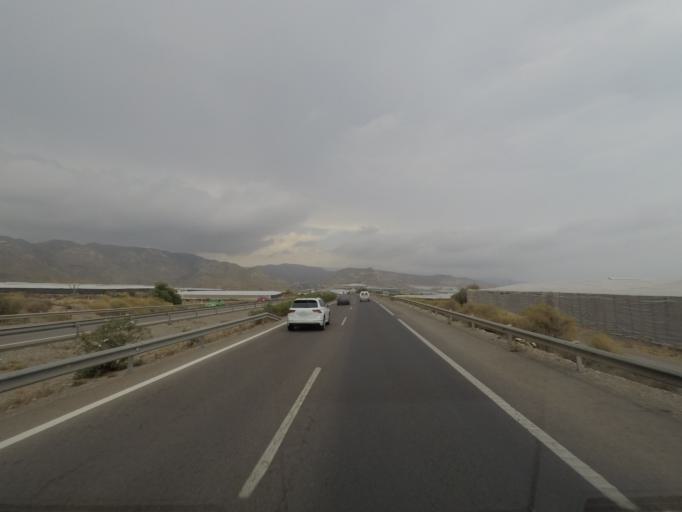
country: ES
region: Andalusia
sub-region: Provincia de Almeria
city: Vicar
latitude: 36.8051
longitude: -2.6725
